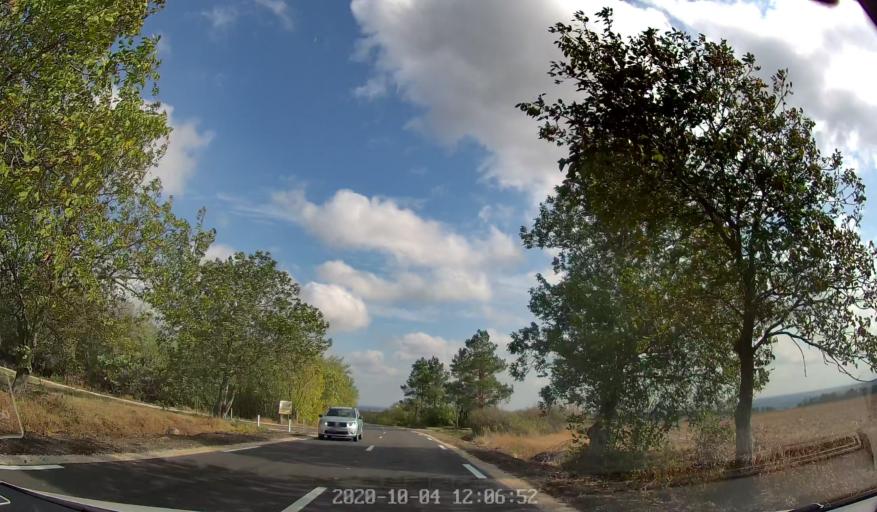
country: MD
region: Rezina
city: Saharna
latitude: 47.5839
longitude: 28.9637
